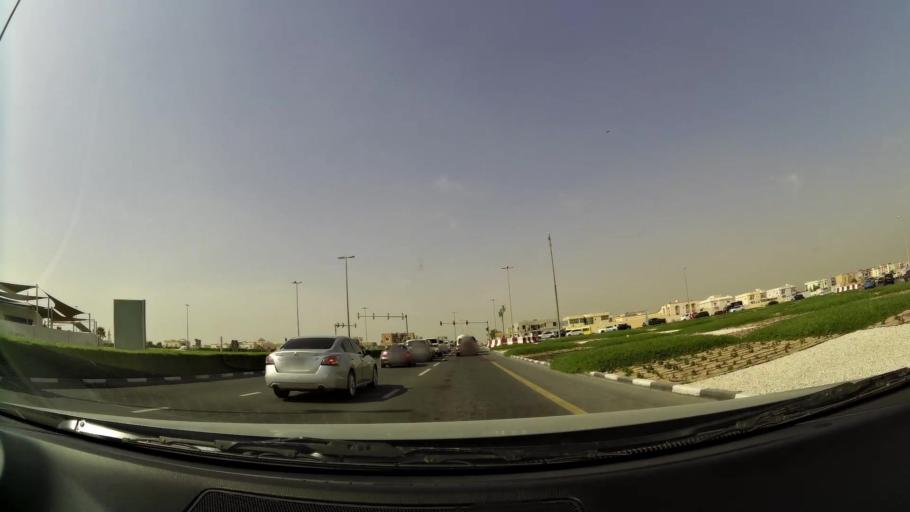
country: AE
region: Ash Shariqah
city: Sharjah
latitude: 25.2097
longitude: 55.4211
